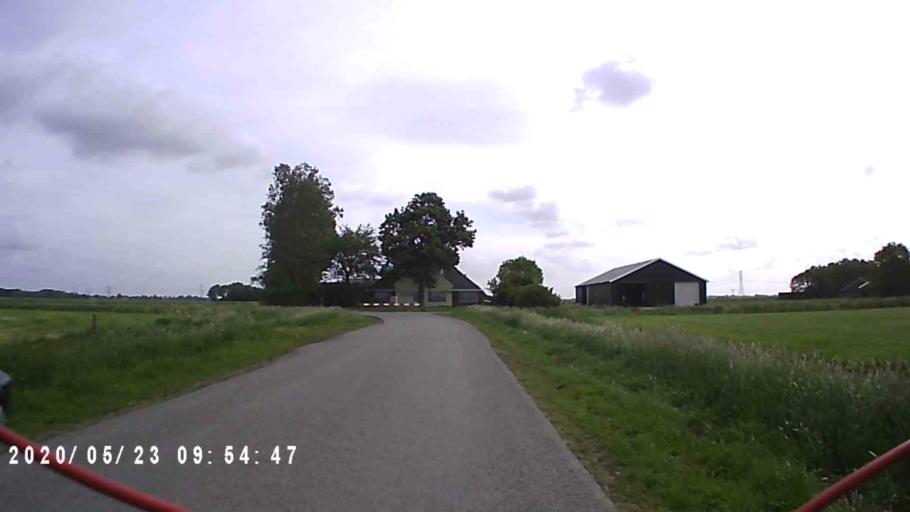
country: NL
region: Groningen
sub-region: Gemeente Appingedam
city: Appingedam
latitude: 53.3034
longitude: 6.8022
